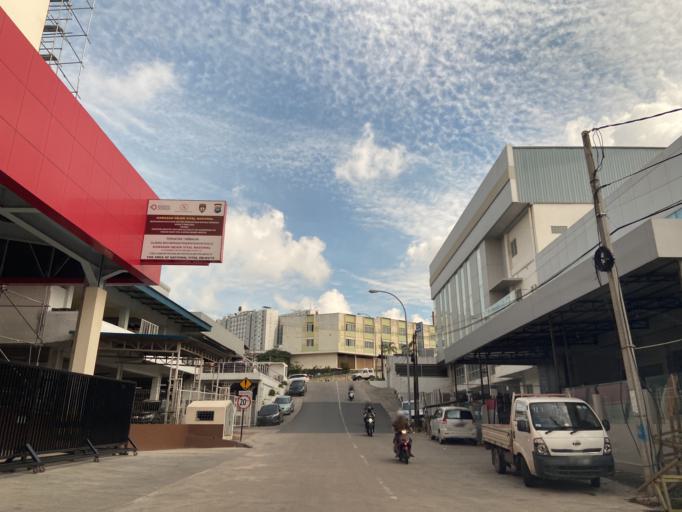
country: SG
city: Singapore
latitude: 1.1412
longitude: 104.0176
